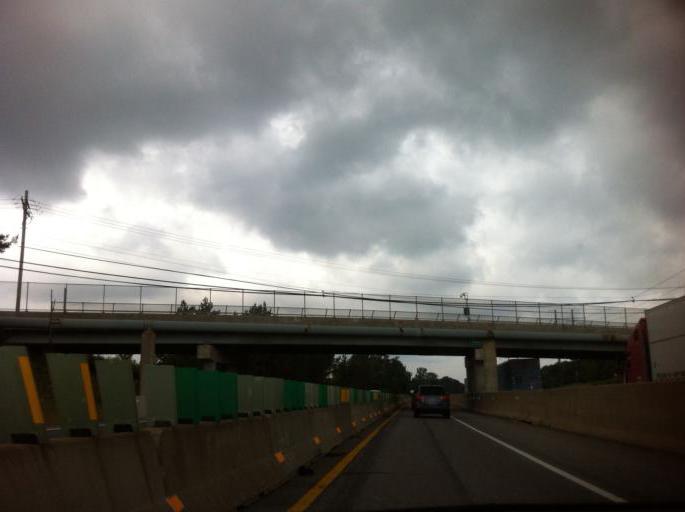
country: US
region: Ohio
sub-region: Cuyahoga County
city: North Royalton
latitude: 41.3183
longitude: -81.7740
